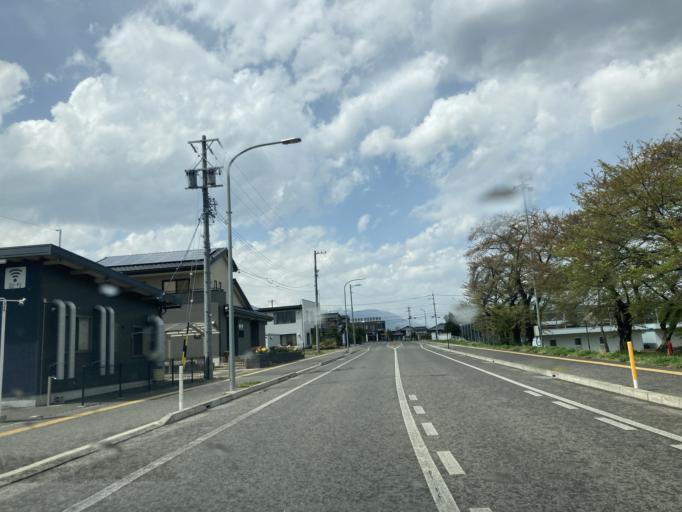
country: JP
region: Nagano
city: Omachi
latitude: 36.4999
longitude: 137.8504
